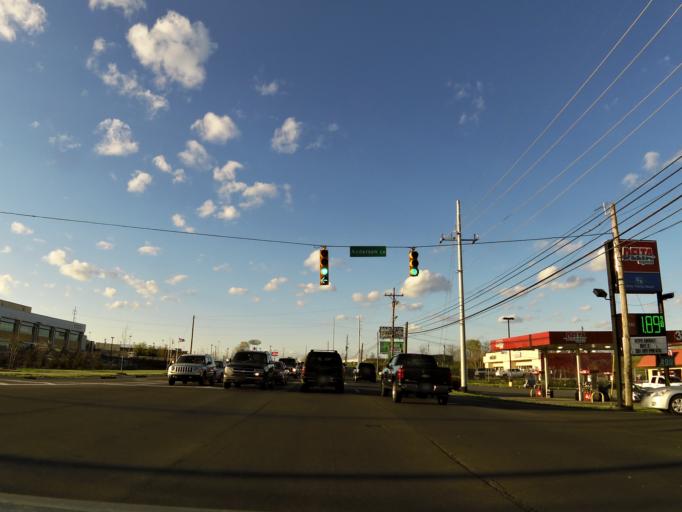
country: US
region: Tennessee
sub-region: Davidson County
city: Goodlettsville
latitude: 36.2719
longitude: -86.6896
